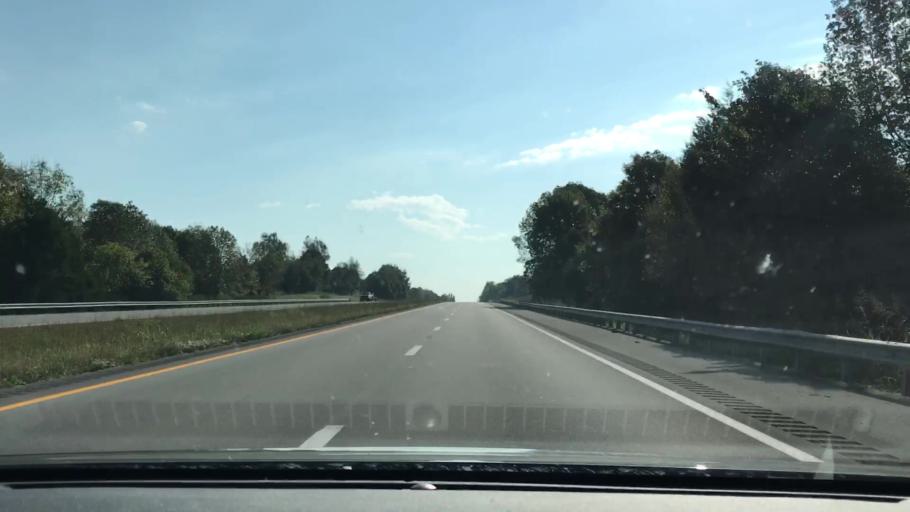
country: US
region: Kentucky
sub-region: Russell County
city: Russell Springs
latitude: 37.0637
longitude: -85.1916
